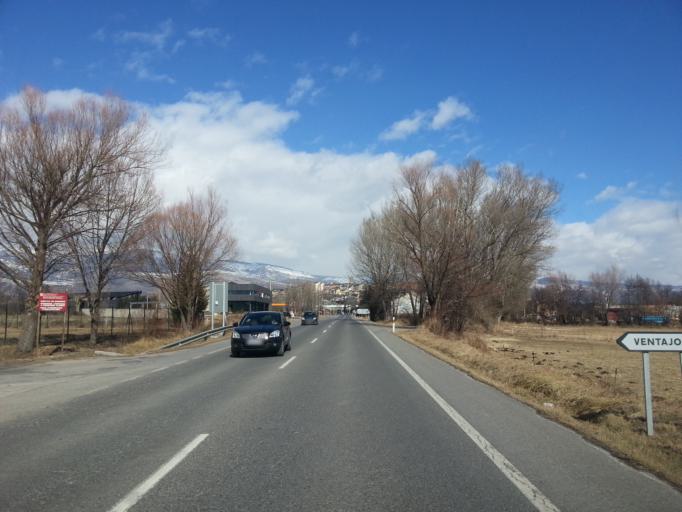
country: ES
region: Catalonia
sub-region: Provincia de Girona
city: Puigcerda
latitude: 42.4201
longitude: 1.9215
